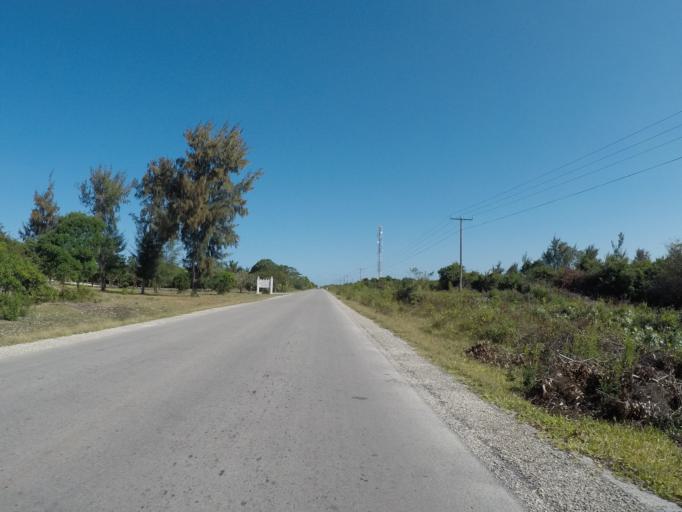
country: TZ
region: Zanzibar Central/South
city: Nganane
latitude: -6.1758
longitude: 39.5270
